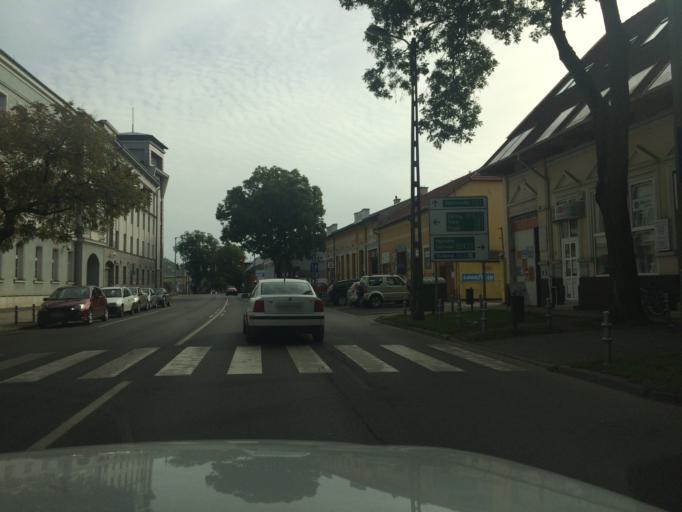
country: HU
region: Szabolcs-Szatmar-Bereg
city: Nyiregyhaza
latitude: 47.9548
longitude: 21.7190
